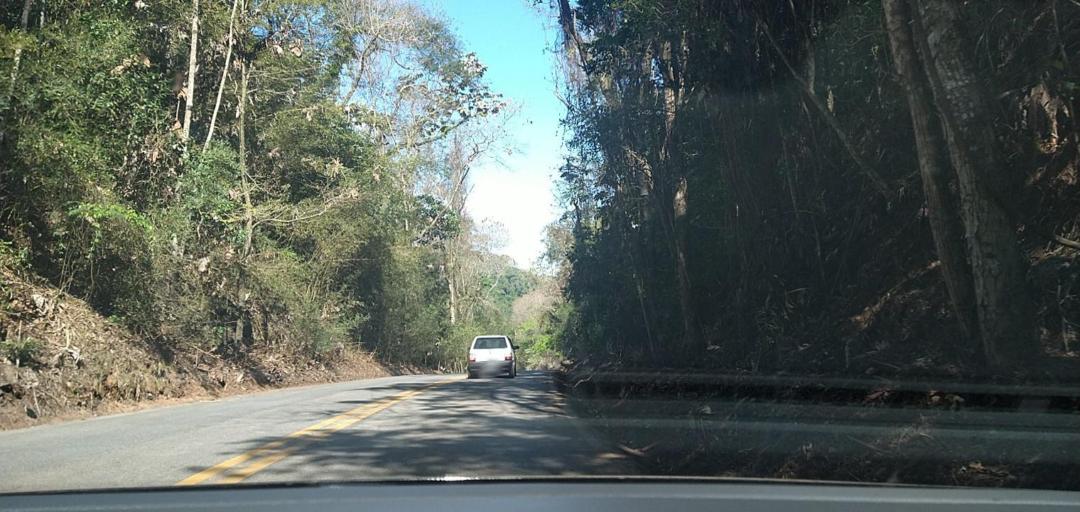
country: BR
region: Minas Gerais
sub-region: Alvinopolis
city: Alvinopolis
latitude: -20.0353
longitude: -43.0373
